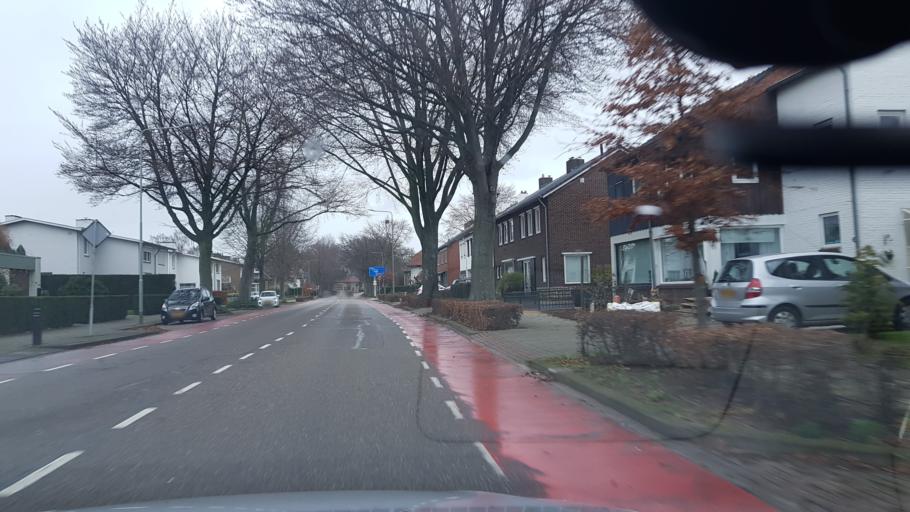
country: NL
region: Limburg
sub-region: Gemeente Beek
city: Beek
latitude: 50.9572
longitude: 5.8335
